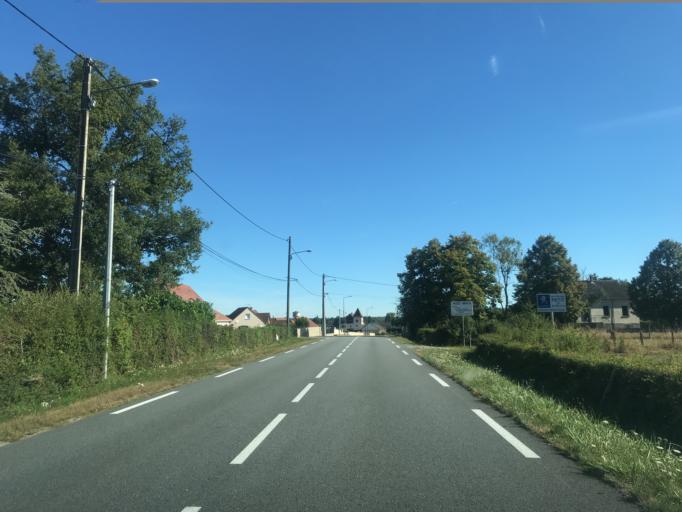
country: FR
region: Limousin
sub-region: Departement de la Creuse
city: Gouzon
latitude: 46.1826
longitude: 2.2305
